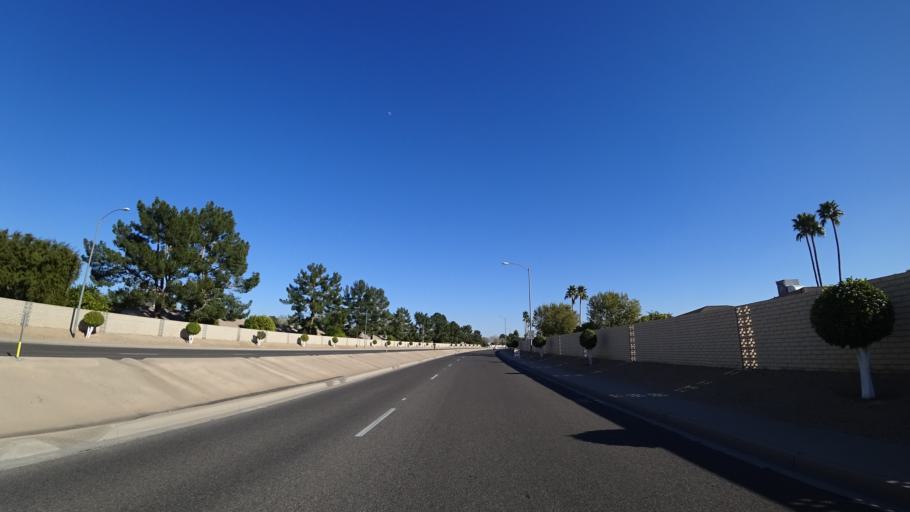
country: US
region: Arizona
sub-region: Maricopa County
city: Sun City West
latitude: 33.6768
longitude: -112.3414
